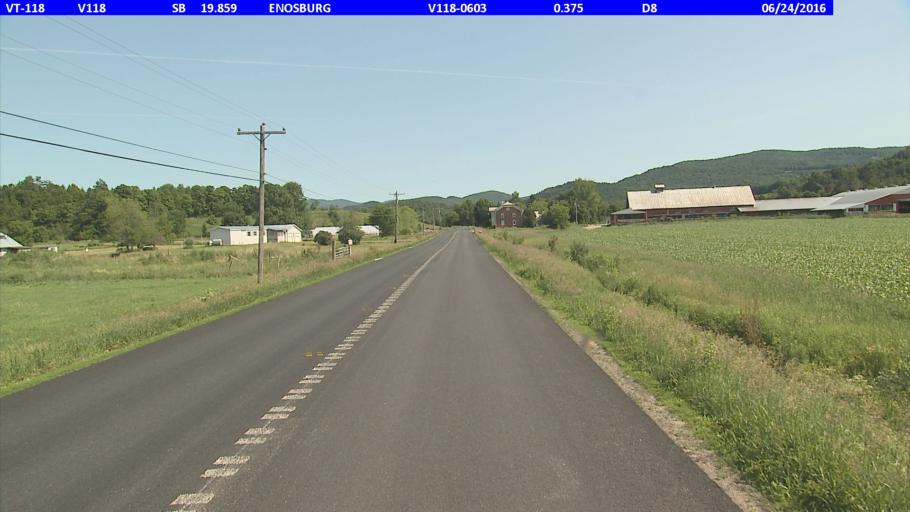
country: US
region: Vermont
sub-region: Franklin County
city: Richford
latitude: 44.9253
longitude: -72.6768
